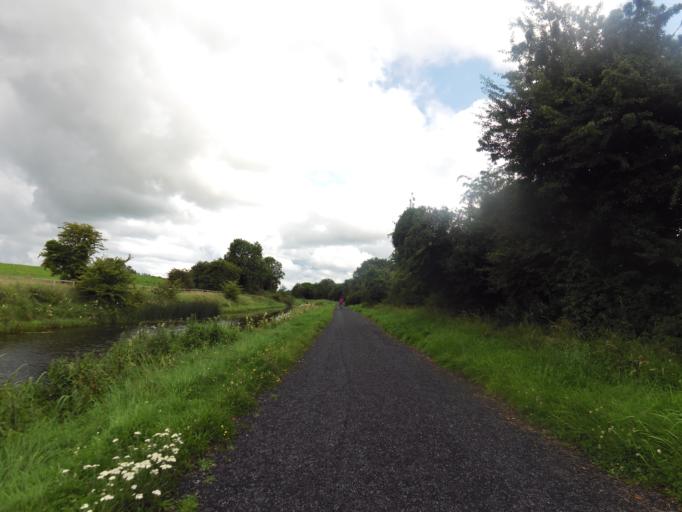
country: IE
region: Leinster
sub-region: An Iarmhi
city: An Muileann gCearr
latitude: 53.5164
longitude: -7.4323
